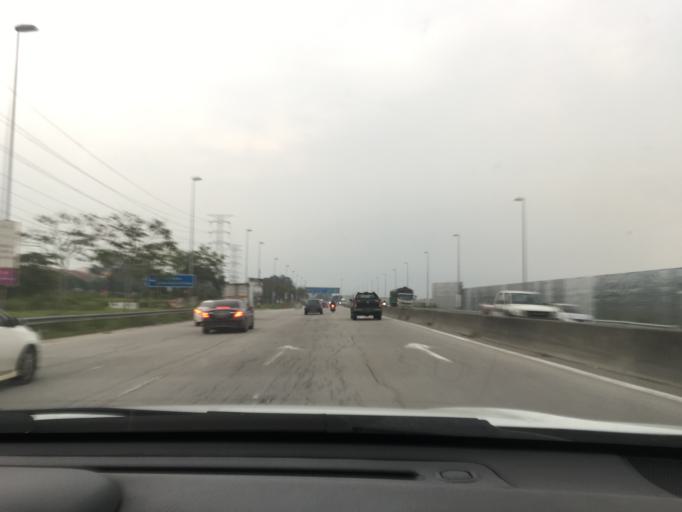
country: MY
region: Selangor
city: Klang
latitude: 3.0969
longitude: 101.4431
